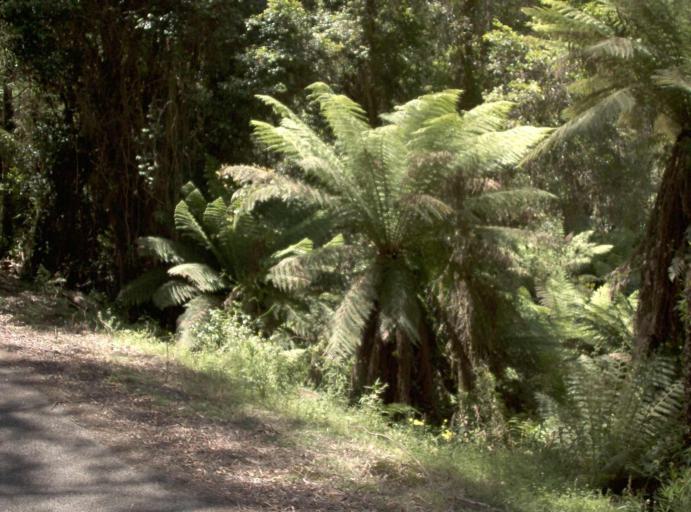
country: AU
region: New South Wales
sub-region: Bombala
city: Bombala
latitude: -37.4543
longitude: 148.9306
